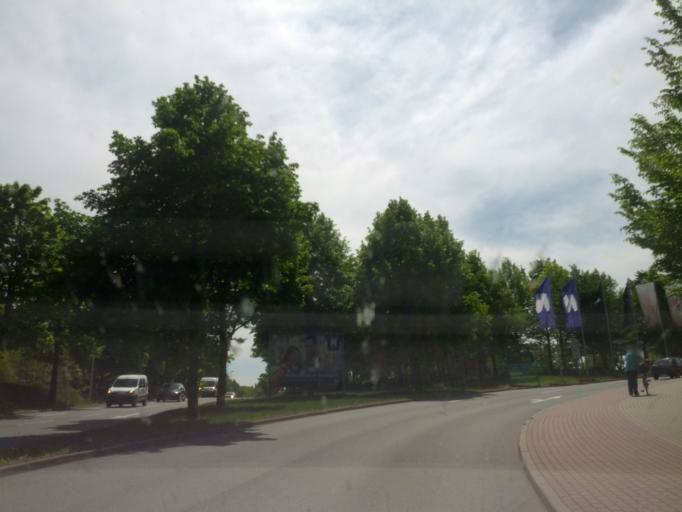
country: DE
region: Saxony
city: Neukirchen
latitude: 50.8073
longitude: 12.8629
